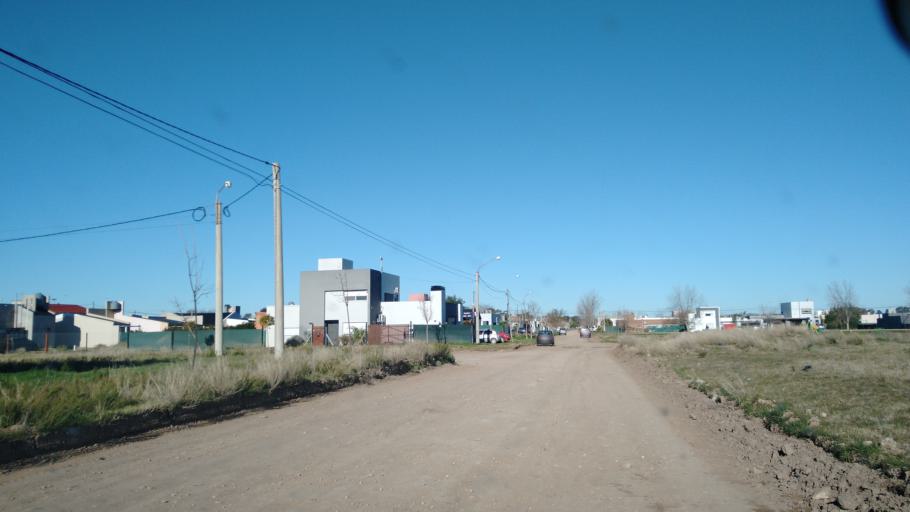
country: AR
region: Buenos Aires
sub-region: Partido de Bahia Blanca
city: Bahia Blanca
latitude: -38.7080
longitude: -62.2042
